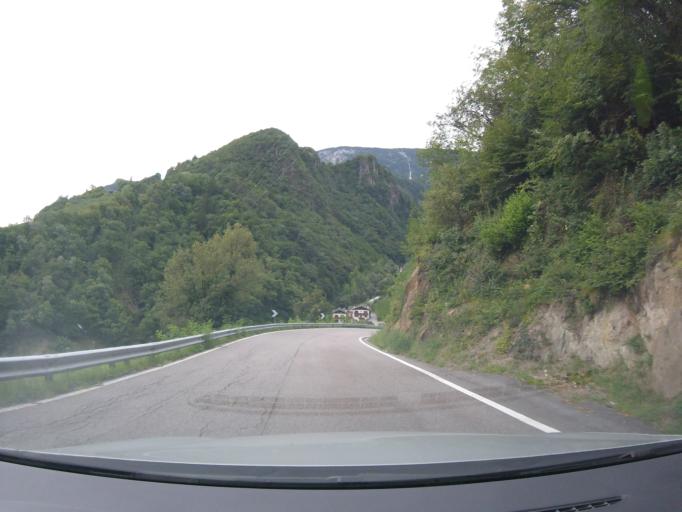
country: IT
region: Trentino-Alto Adige
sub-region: Bolzano
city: Nalles
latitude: 46.5452
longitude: 11.1954
